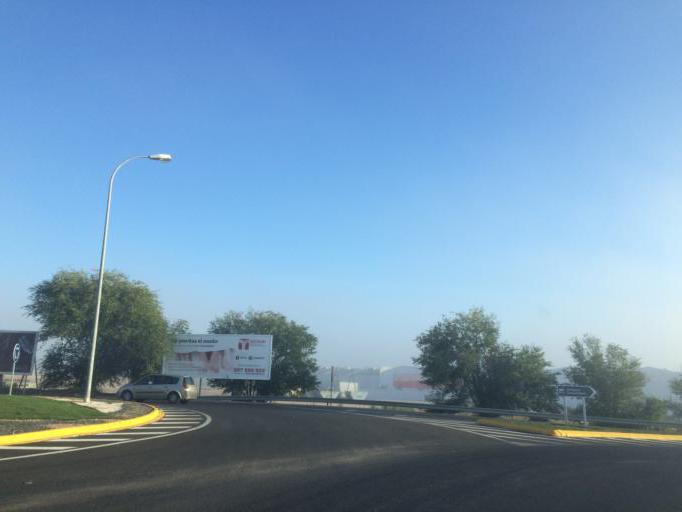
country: ES
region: Castille-La Mancha
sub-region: Provincia de Albacete
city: Albacete
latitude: 39.0082
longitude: -1.8887
